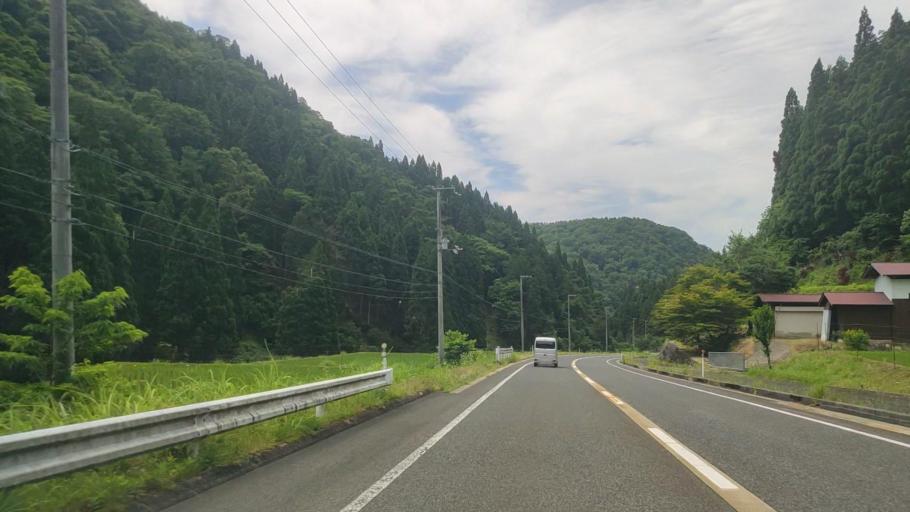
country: JP
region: Hyogo
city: Toyooka
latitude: 35.4868
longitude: 134.6158
